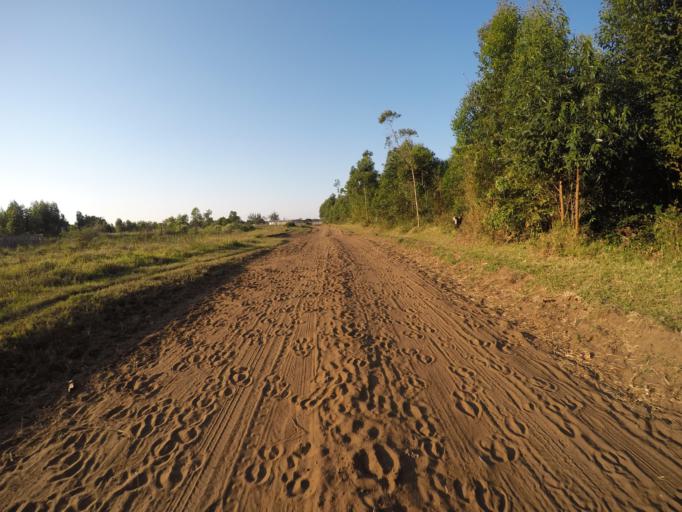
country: ZA
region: KwaZulu-Natal
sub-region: uThungulu District Municipality
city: KwaMbonambi
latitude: -28.6903
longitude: 32.2046
